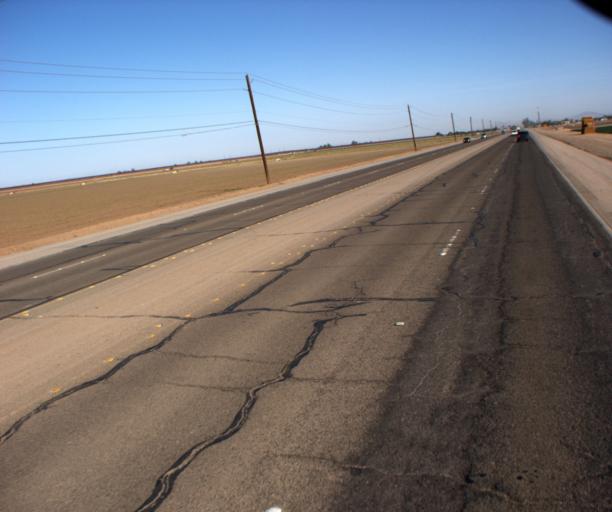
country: US
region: Arizona
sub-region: Yuma County
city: San Luis
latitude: 32.5352
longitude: -114.7868
